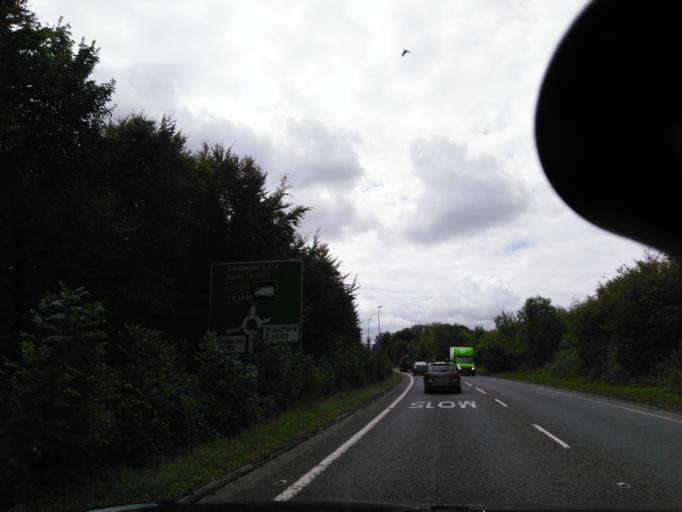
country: GB
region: England
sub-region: Dorset
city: Blandford Forum
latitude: 50.8590
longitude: -2.1494
